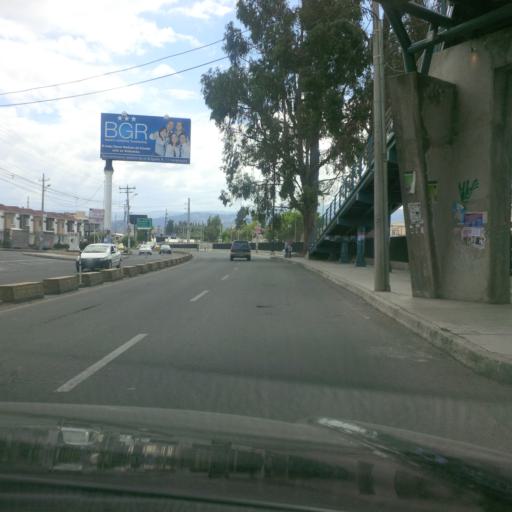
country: EC
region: Chimborazo
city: Riobamba
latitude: -1.6535
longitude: -78.6445
